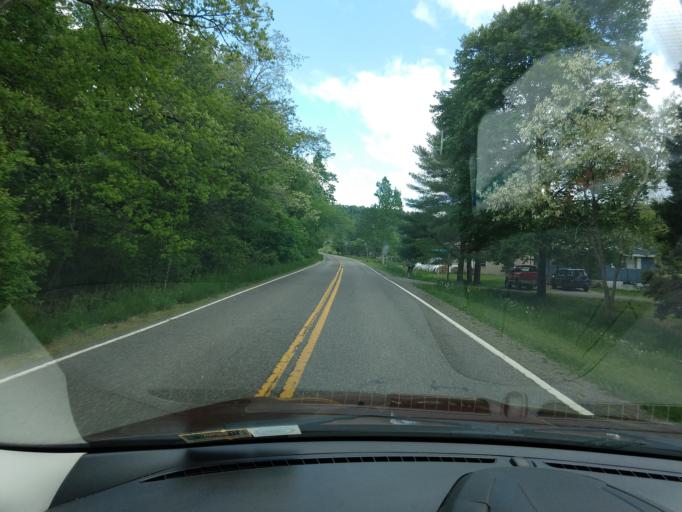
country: US
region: Virginia
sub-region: City of Galax
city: Galax
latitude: 36.7903
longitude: -80.9850
